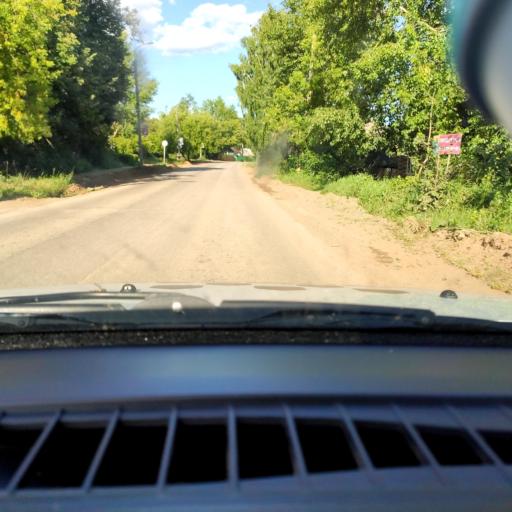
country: RU
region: Perm
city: Ocher
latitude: 57.8828
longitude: 54.7317
